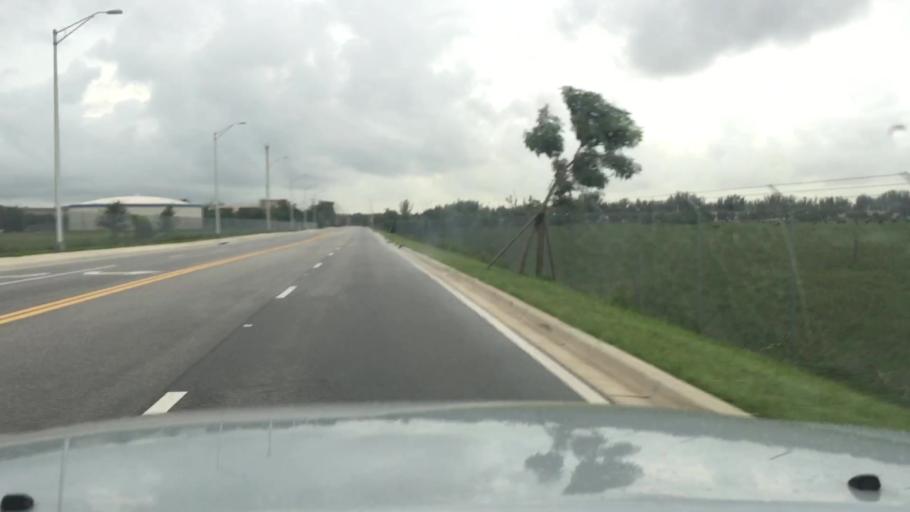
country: US
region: Florida
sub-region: Miami-Dade County
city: Doral
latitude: 25.8037
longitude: -80.3453
